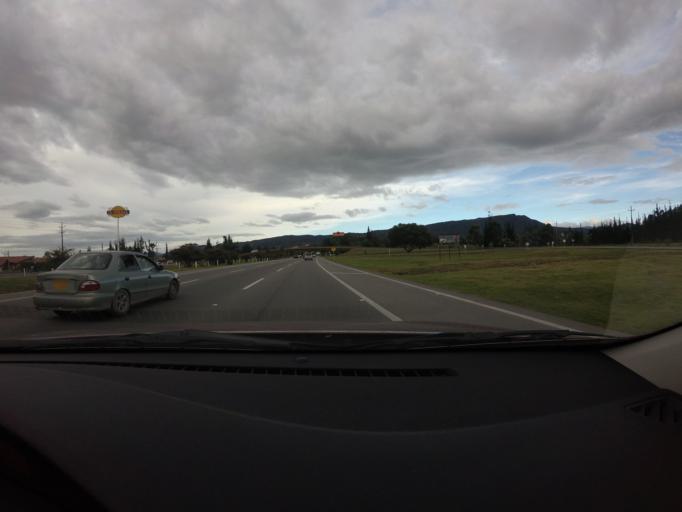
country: CO
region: Cundinamarca
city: Sopo
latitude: 4.9392
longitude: -73.9682
